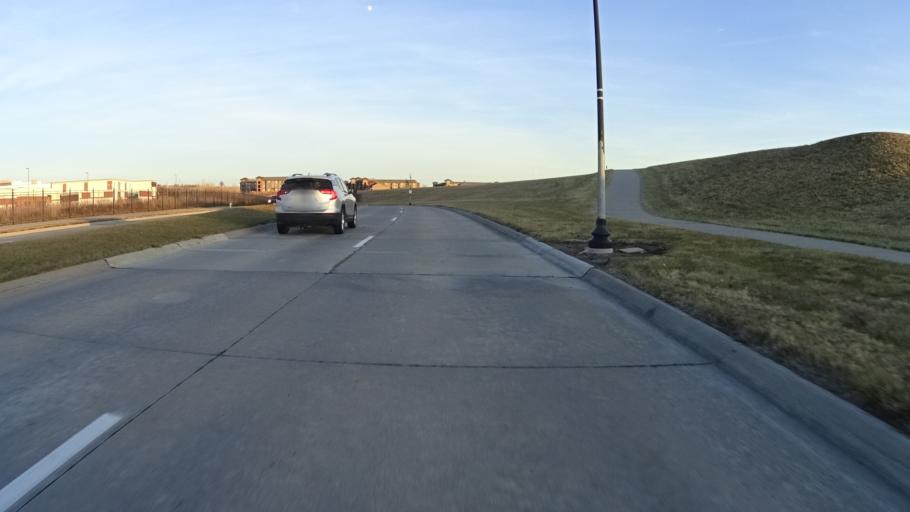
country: US
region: Nebraska
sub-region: Sarpy County
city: Papillion
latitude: 41.1320
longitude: -96.0321
